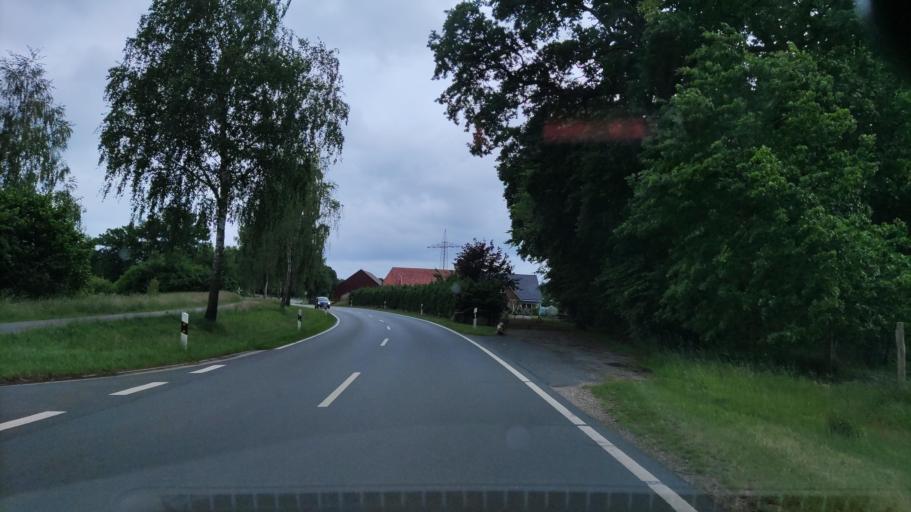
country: DE
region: Lower Saxony
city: Schneverdingen
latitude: 53.1141
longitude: 9.7659
